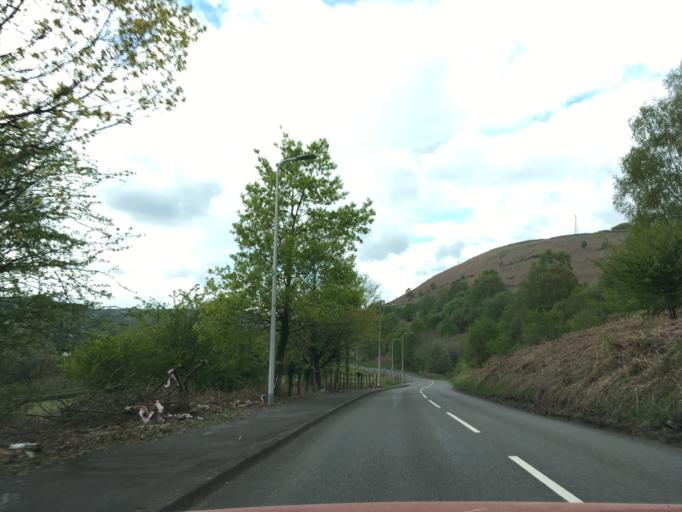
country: GB
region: Wales
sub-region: Merthyr Tydfil County Borough
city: Treharris
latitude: 51.6885
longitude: -3.2986
